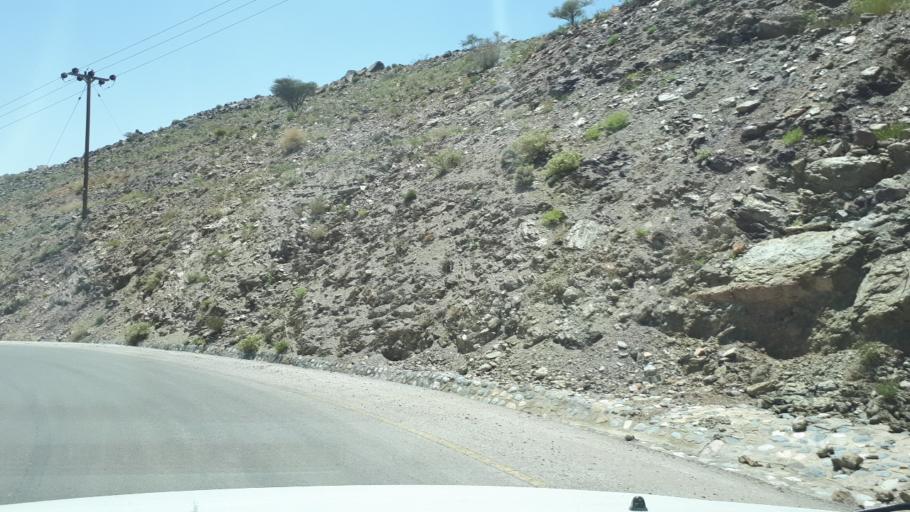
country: OM
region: Muhafazat ad Dakhiliyah
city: Bahla'
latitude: 23.2123
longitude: 57.1464
